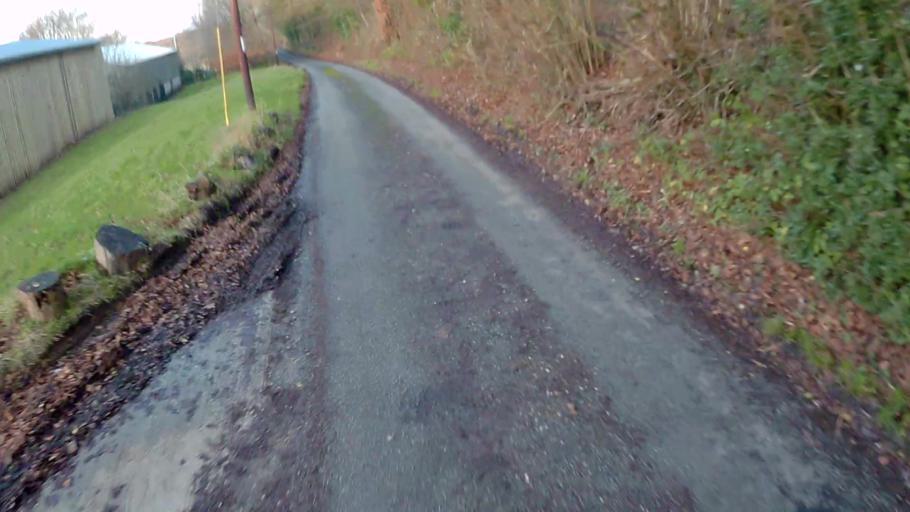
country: GB
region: England
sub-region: Hampshire
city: Overton
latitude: 51.2139
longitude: -1.2456
